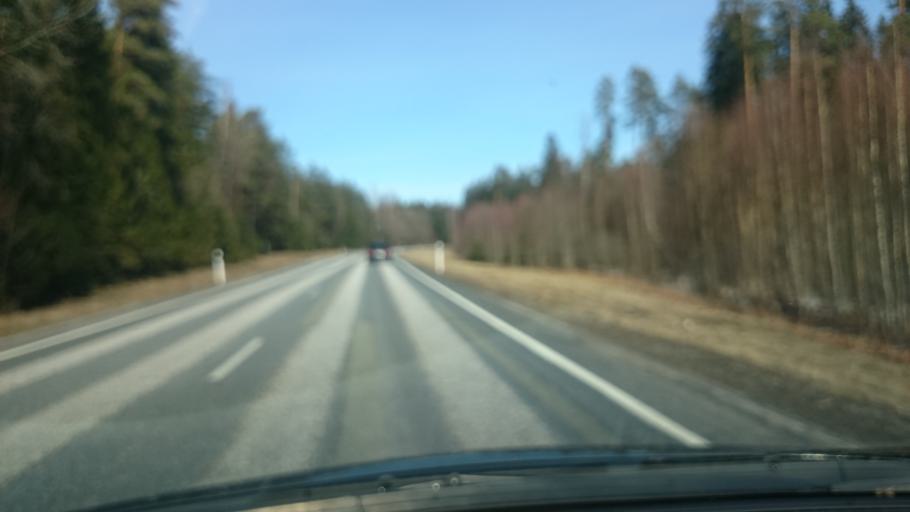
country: EE
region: Jaervamaa
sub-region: Tueri vald
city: Sarevere
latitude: 58.7388
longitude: 25.3012
